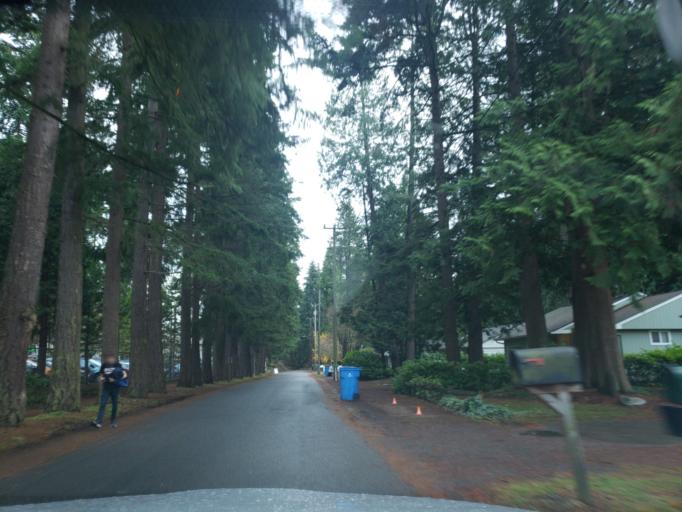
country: US
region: Washington
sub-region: Snohomish County
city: Esperance
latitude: 47.7701
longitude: -122.3559
